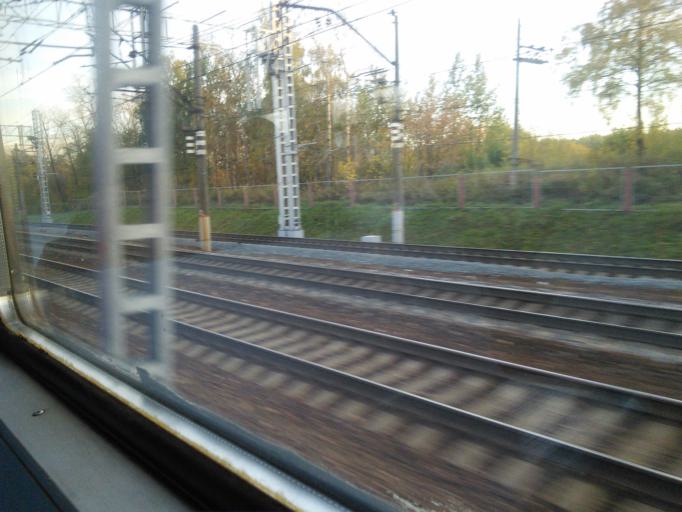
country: RU
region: Moscow
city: Khimki
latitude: 55.9211
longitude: 37.3891
